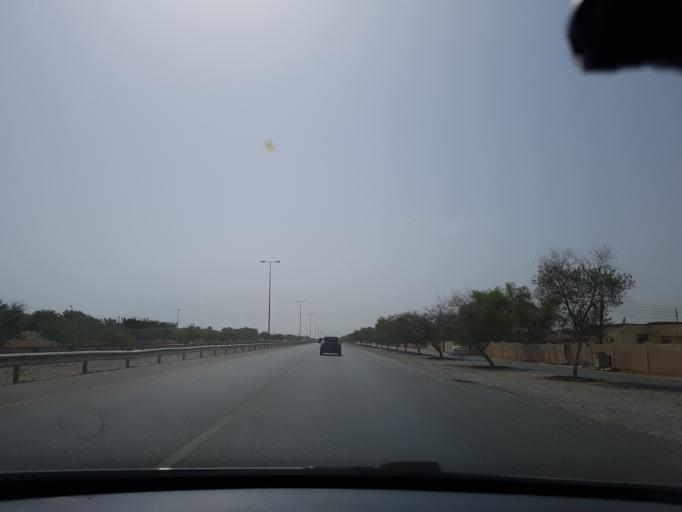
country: OM
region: Al Batinah
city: Al Khaburah
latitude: 23.9387
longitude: 57.1277
